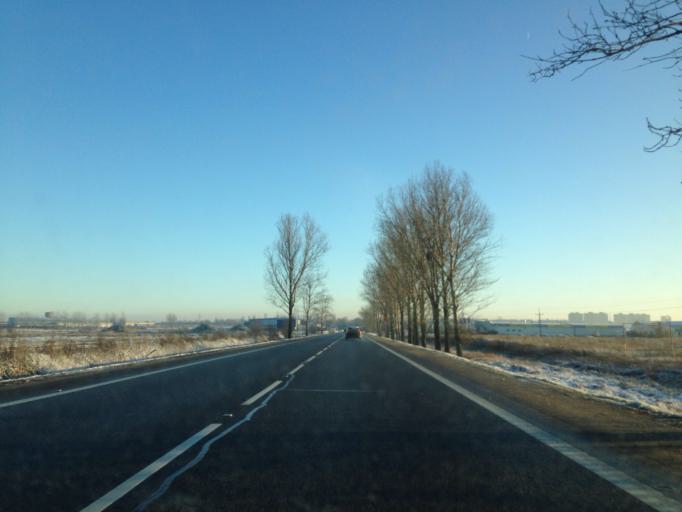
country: PL
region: Pomeranian Voivodeship
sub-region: Powiat tczewski
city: Tczew
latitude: 54.1141
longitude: 18.7573
